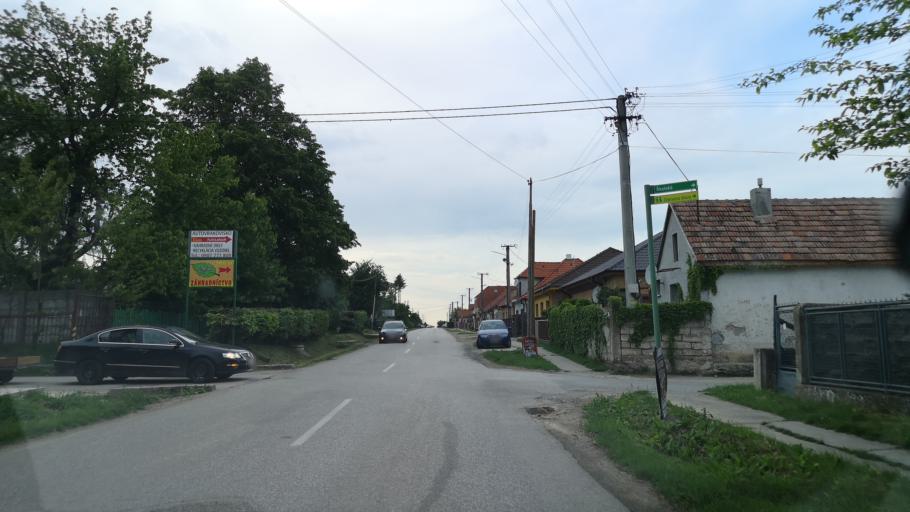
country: SK
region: Nitriansky
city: Sellye
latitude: 48.2439
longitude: 17.9100
